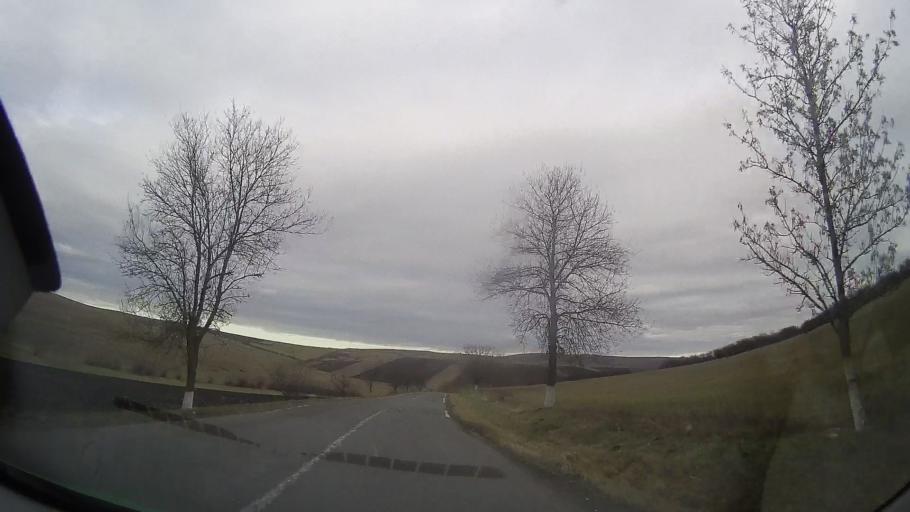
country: RO
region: Mures
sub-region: Comuna Faragau
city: Faragau
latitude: 46.7600
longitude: 24.5409
